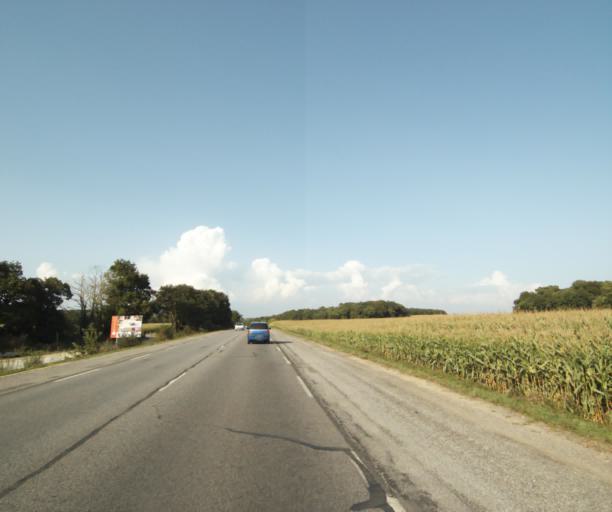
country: FR
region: Brittany
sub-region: Departement du Morbihan
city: Riantec
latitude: 47.7537
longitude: -3.2886
